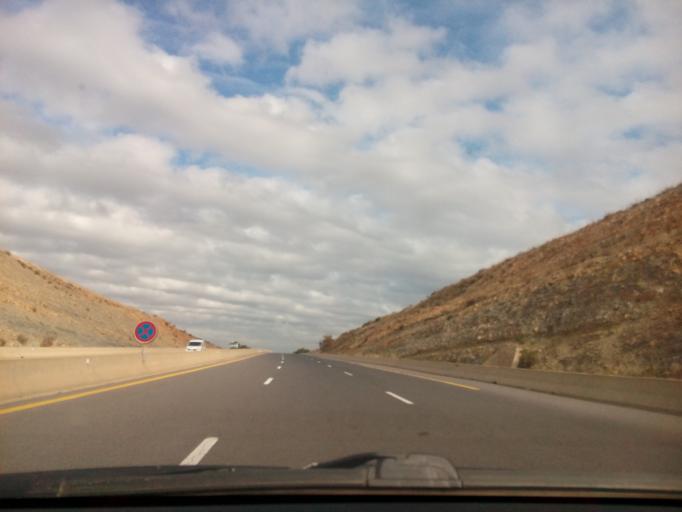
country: DZ
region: Tlemcen
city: Chetouane
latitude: 34.9436
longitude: -1.3097
